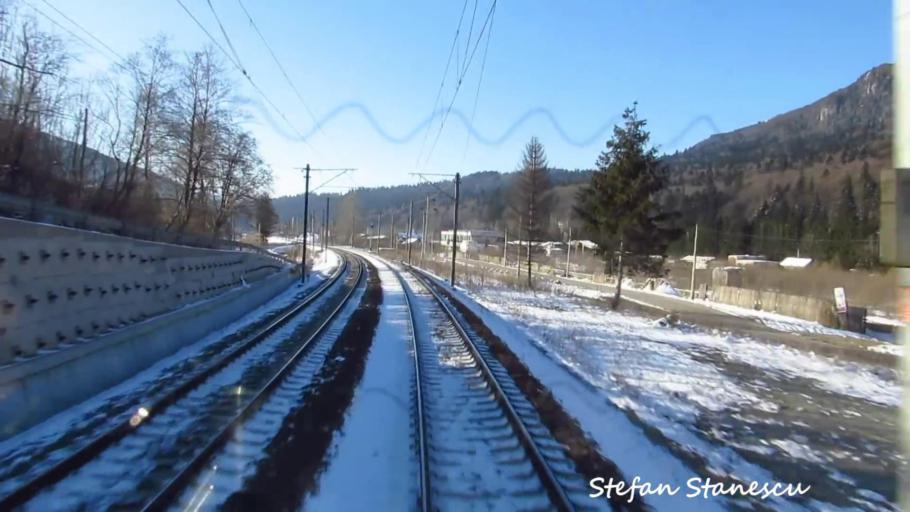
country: RO
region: Prahova
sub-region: Oras Busteni
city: Poiana Tapului
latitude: 45.3800
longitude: 25.5412
